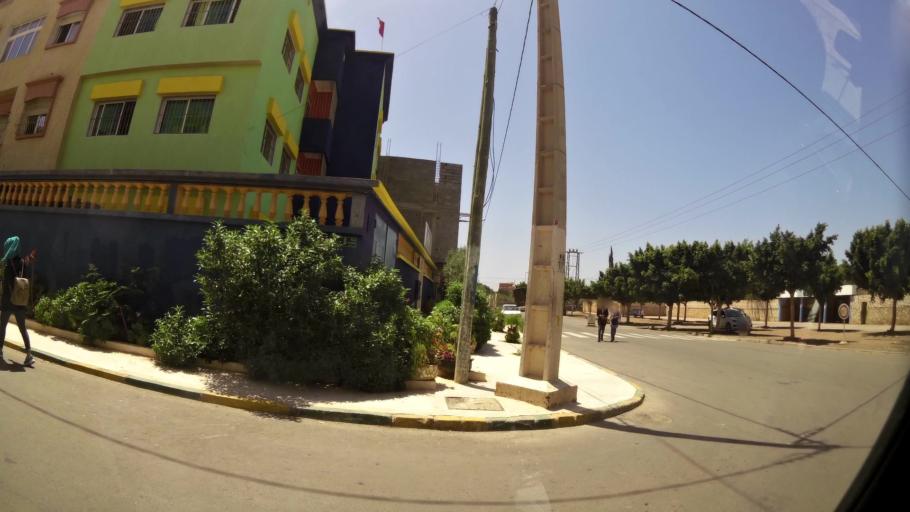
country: MA
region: Souss-Massa-Draa
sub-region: Inezgane-Ait Mellou
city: Inezgane
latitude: 30.3513
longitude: -9.4856
